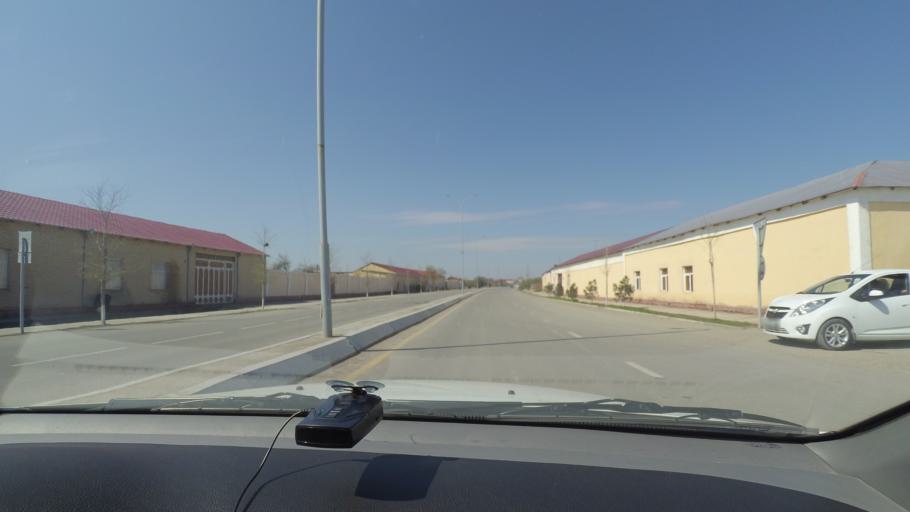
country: UZ
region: Bukhara
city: Kogon
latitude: 39.8000
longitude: 64.5333
